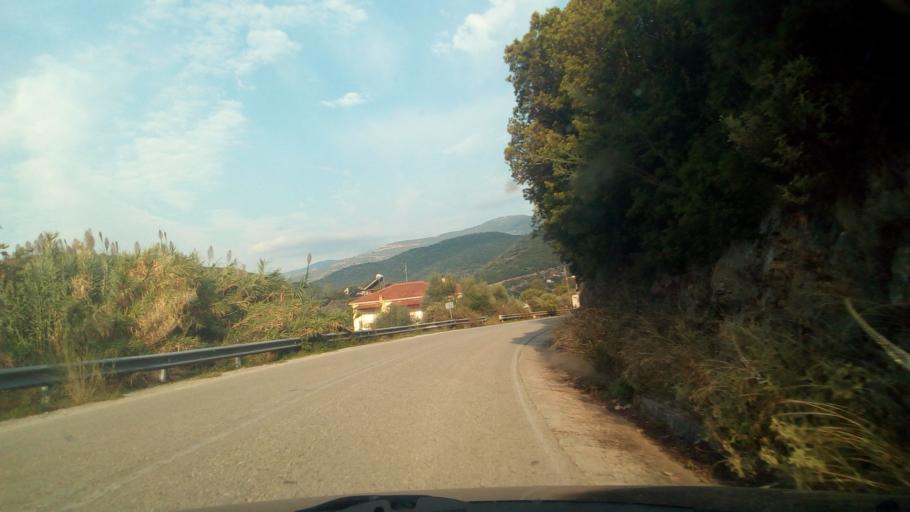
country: GR
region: West Greece
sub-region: Nomos Aitolias kai Akarnanias
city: Nafpaktos
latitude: 38.4229
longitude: 21.9169
